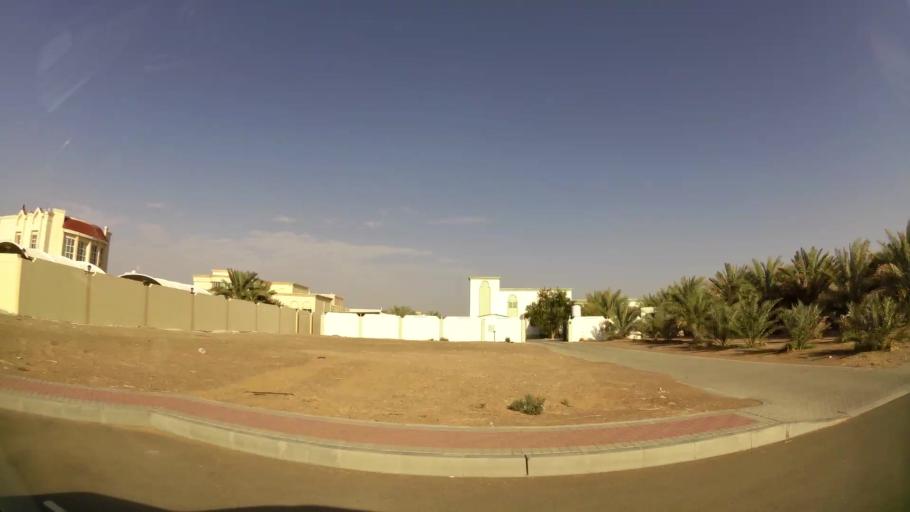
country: AE
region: Abu Dhabi
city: Al Ain
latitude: 24.0565
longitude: 55.8415
